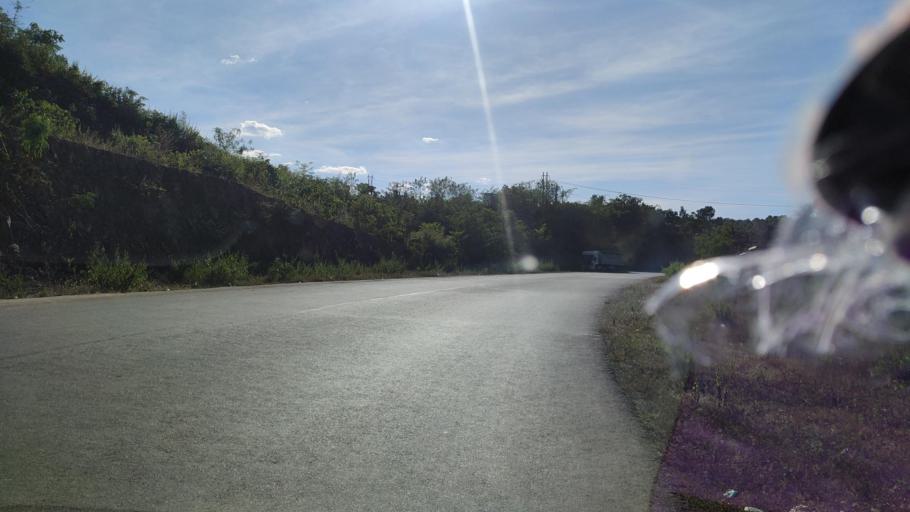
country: MM
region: Mandalay
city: Yamethin
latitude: 20.8077
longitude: 96.3604
